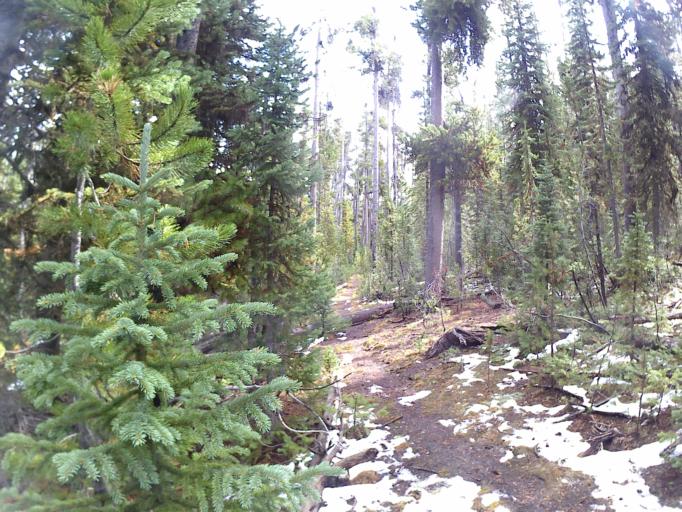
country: US
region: Montana
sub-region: Gallatin County
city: West Yellowstone
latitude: 44.4325
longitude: -110.7394
